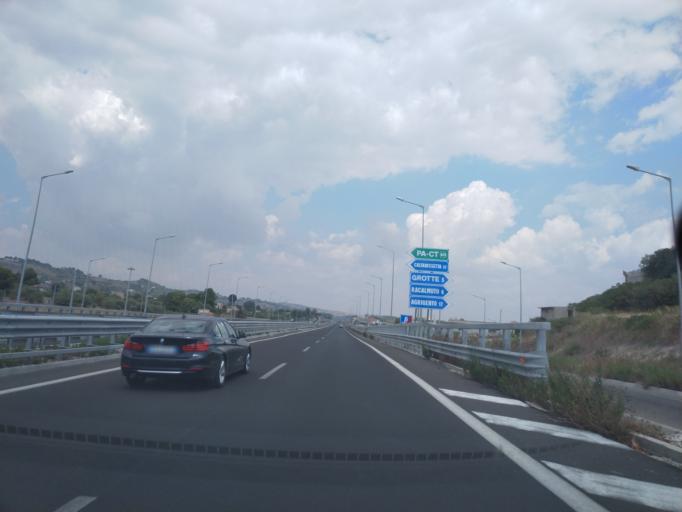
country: IT
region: Sicily
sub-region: Agrigento
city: Racalmuto
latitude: 37.3735
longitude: 13.7165
